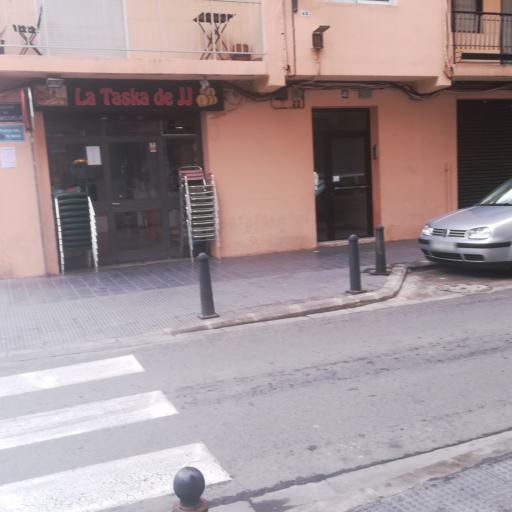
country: ES
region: Valencia
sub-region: Provincia de Valencia
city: Valencia
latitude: 39.4550
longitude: -0.3873
